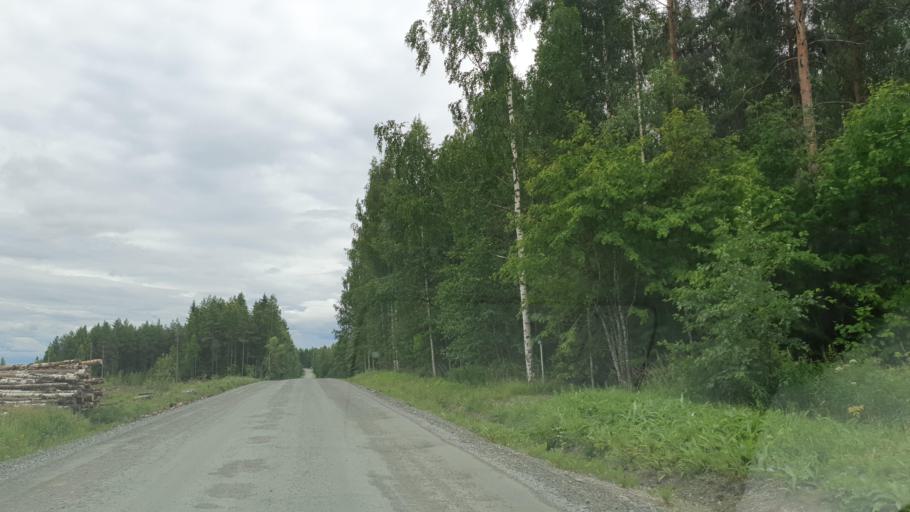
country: FI
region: Northern Savo
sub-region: Ylae-Savo
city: Iisalmi
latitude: 63.5244
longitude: 27.0925
